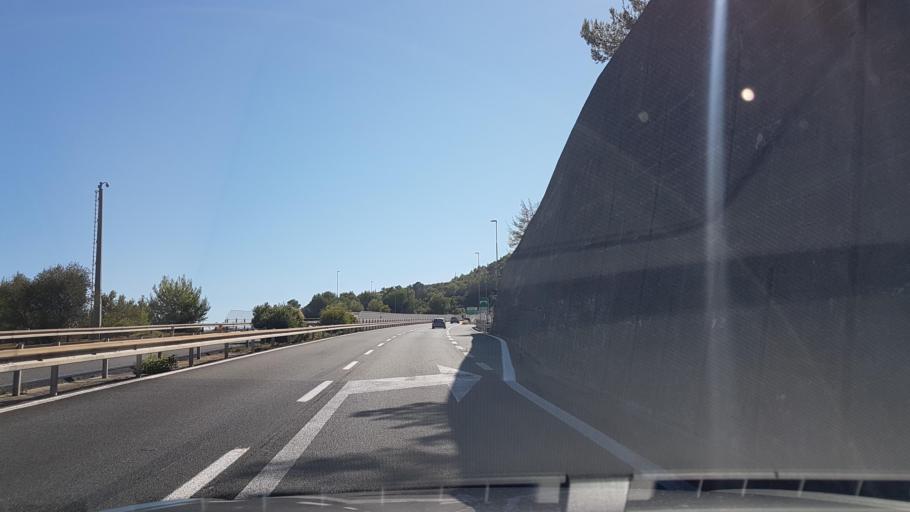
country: IT
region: Liguria
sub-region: Provincia di Imperia
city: Taggia
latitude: 43.8511
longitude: 7.8393
